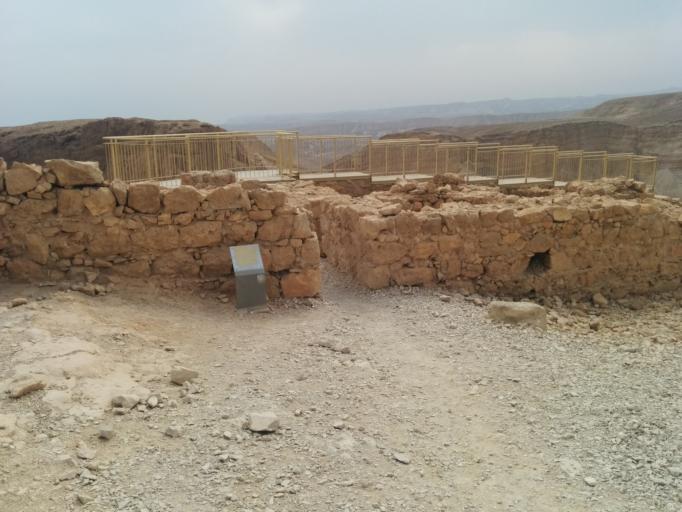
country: IL
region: Southern District
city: `En Boqeq
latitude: 31.3128
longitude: 35.3528
